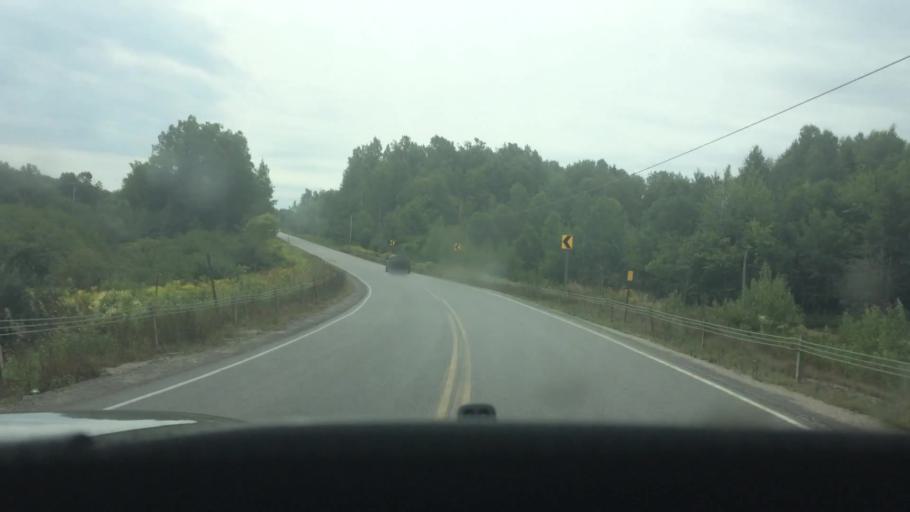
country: US
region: New York
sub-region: St. Lawrence County
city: Canton
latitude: 44.4847
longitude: -75.2483
